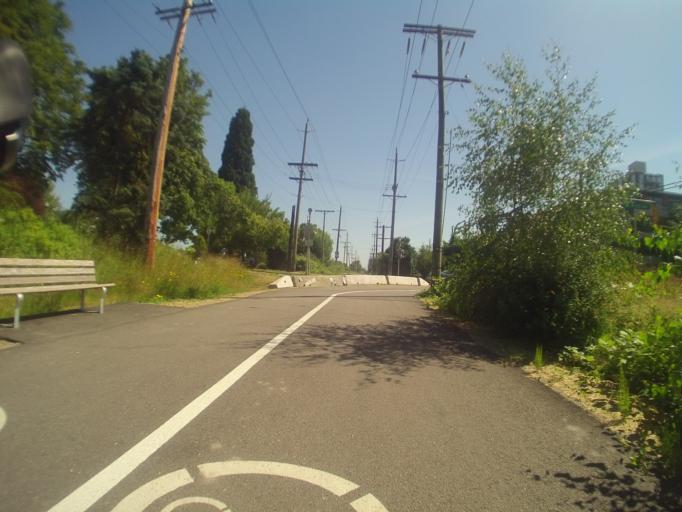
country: CA
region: British Columbia
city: Vancouver
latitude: 49.2386
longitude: -123.1553
